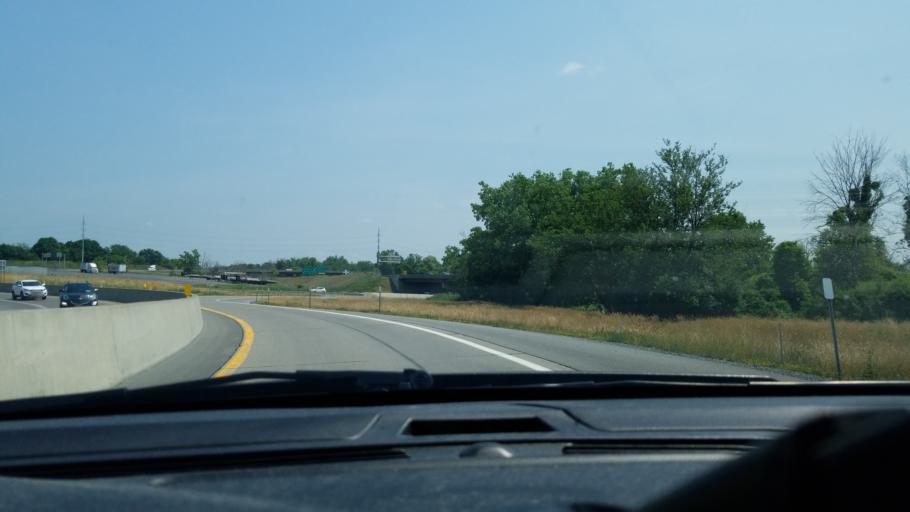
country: US
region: New York
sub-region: Onondaga County
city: Galeville
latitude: 43.0922
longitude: -76.1662
